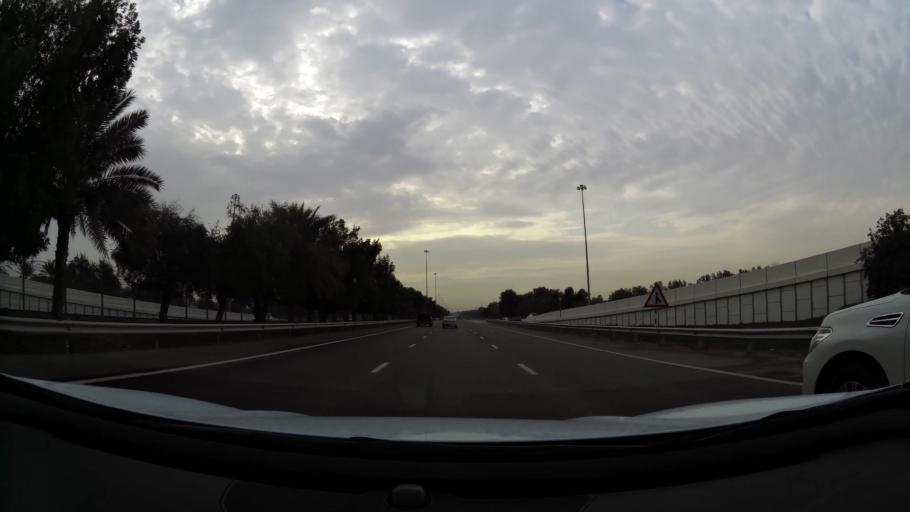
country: AE
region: Abu Dhabi
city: Abu Dhabi
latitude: 24.2800
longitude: 54.6489
